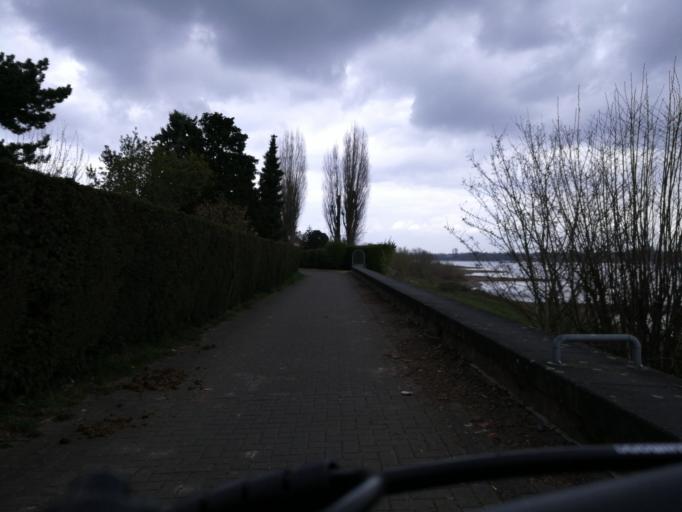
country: DE
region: North Rhine-Westphalia
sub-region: Regierungsbezirk Dusseldorf
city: Dusseldorf
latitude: 51.1587
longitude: 6.7908
